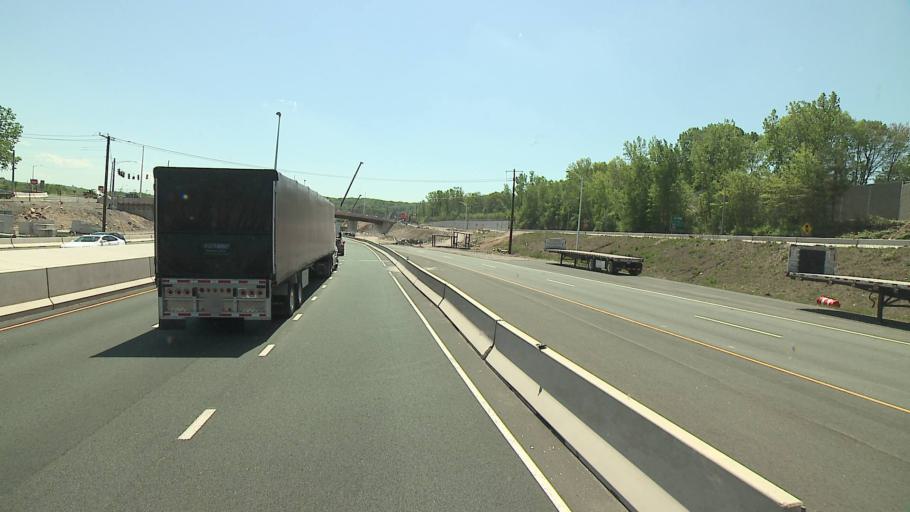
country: US
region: Connecticut
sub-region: New Haven County
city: Waterbury
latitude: 41.5431
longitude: -73.0247
